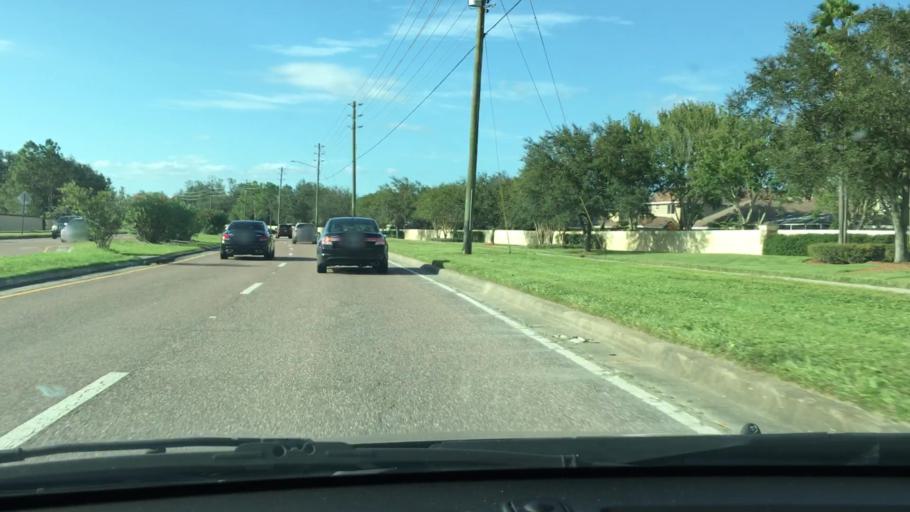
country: US
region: Florida
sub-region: Pasco County
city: Land O' Lakes
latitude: 28.2083
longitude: -82.4337
